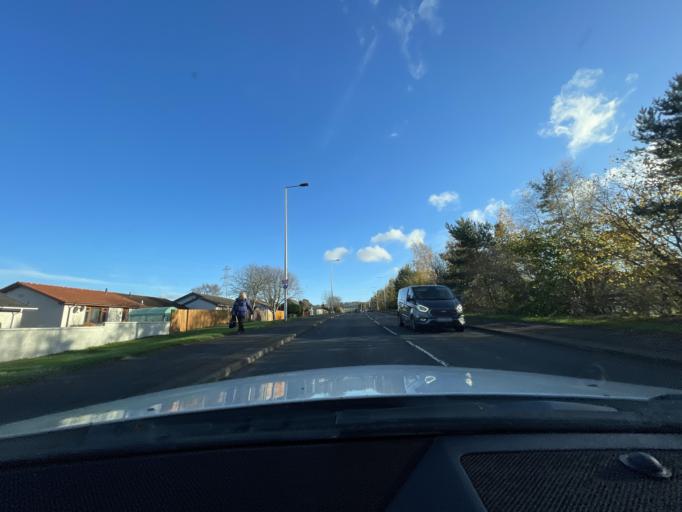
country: GB
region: Scotland
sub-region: Highland
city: Inverness
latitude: 57.4489
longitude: -4.2433
